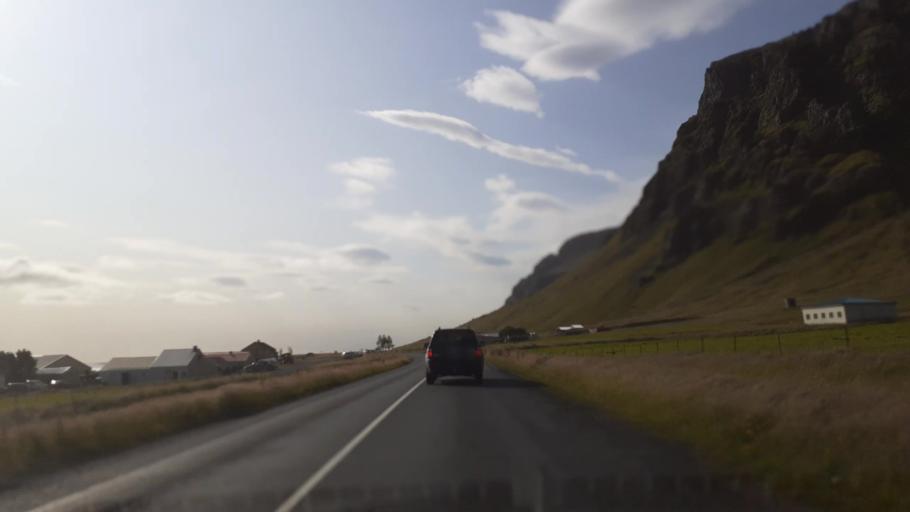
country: IS
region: South
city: Vestmannaeyjar
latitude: 63.5426
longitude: -19.6935
